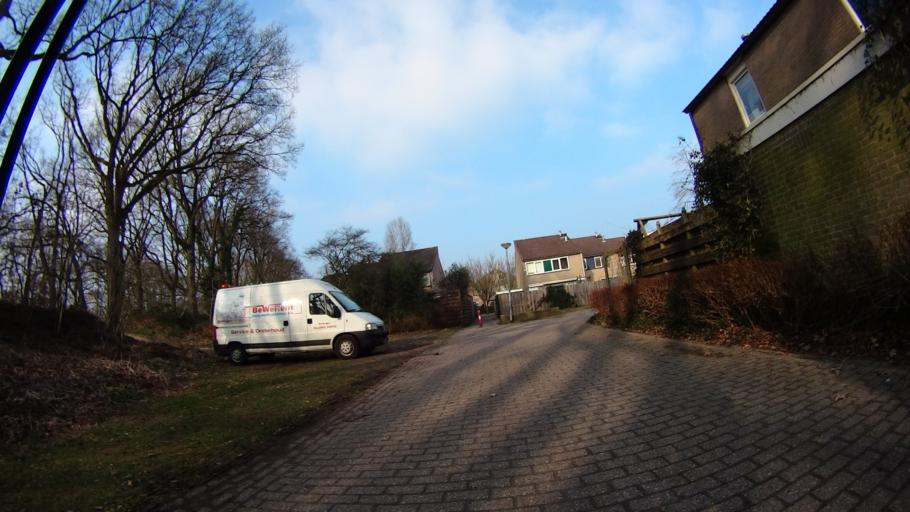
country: NL
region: Drenthe
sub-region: Gemeente Emmen
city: Emmen
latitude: 52.7627
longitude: 6.8896
